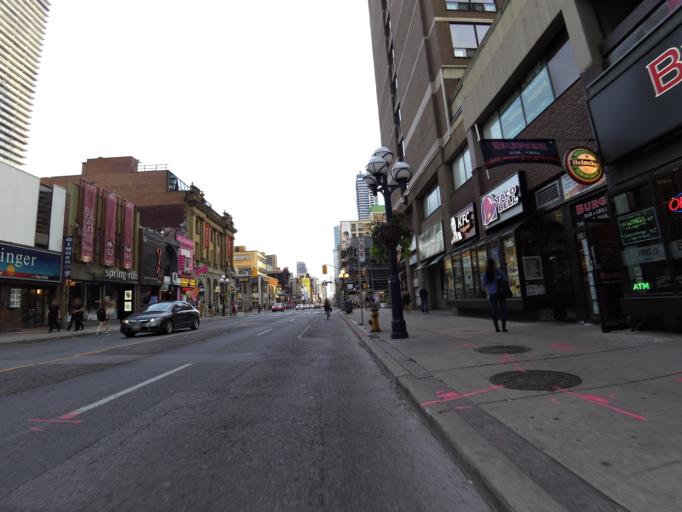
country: CA
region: Ontario
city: Toronto
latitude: 43.6692
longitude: -79.3864
